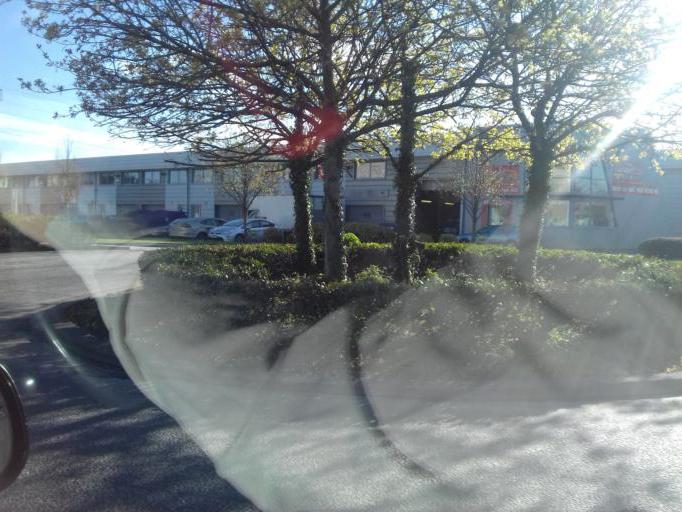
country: IE
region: Leinster
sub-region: Fingal County
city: Blanchardstown
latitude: 53.4080
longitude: -6.3421
